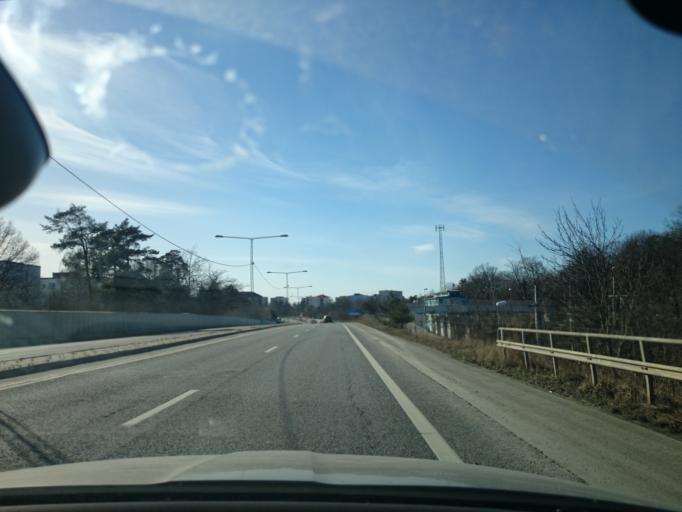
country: SE
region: Stockholm
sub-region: Haninge Kommun
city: Handen
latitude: 59.2364
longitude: 18.1081
